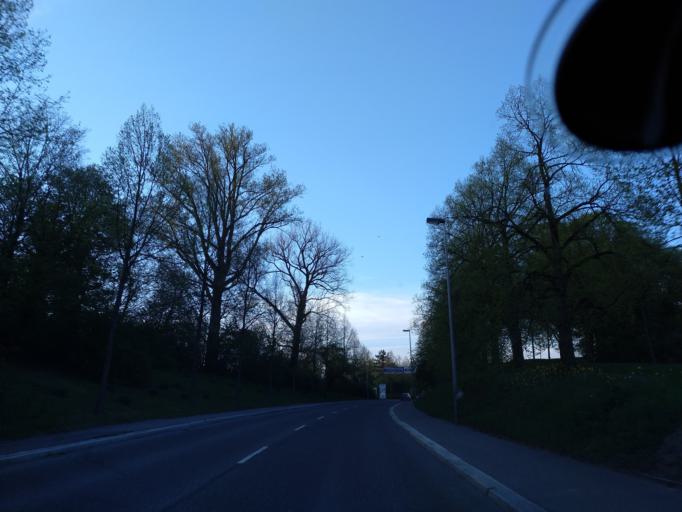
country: DE
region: Baden-Wuerttemberg
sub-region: Regierungsbezirk Stuttgart
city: Crailsheim
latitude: 49.1447
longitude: 10.0719
